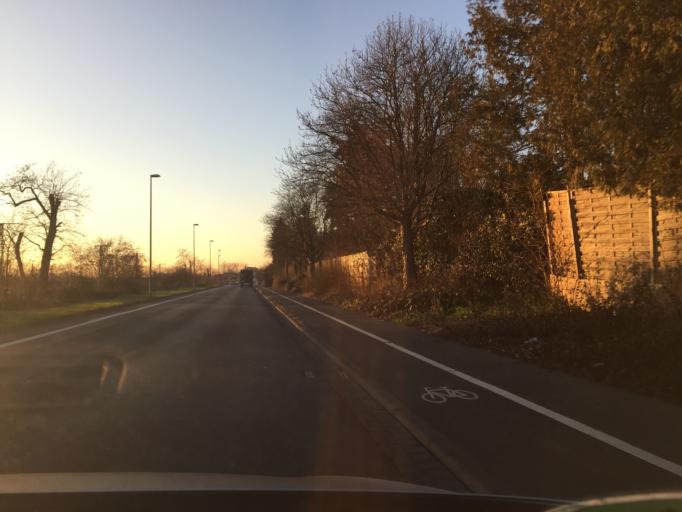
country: DE
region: Bavaria
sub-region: Regierungsbezirk Unterfranken
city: Aschaffenburg
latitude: 49.9819
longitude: 9.1229
